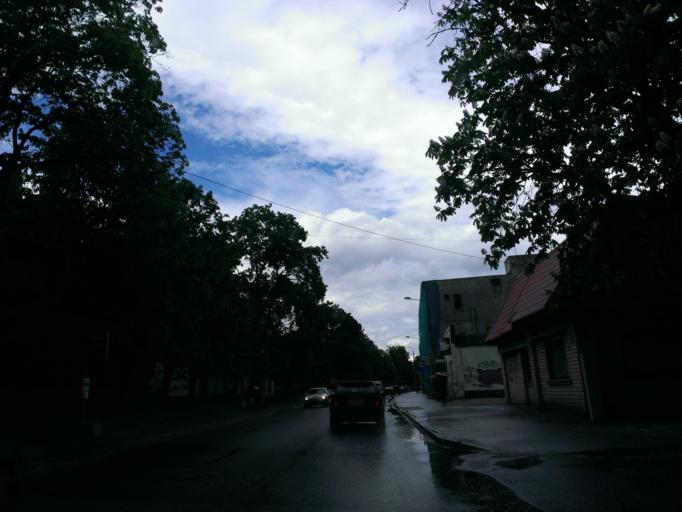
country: LV
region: Riga
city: Riga
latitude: 56.9220
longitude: 24.0960
